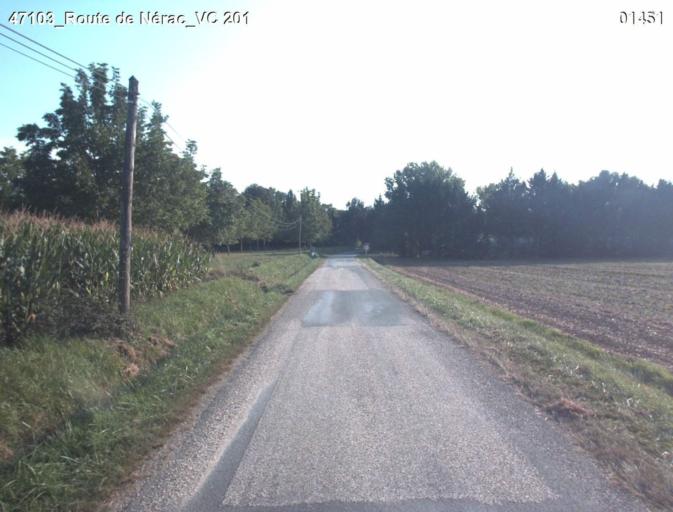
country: FR
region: Aquitaine
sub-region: Departement du Lot-et-Garonne
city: Nerac
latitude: 44.0874
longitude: 0.3327
